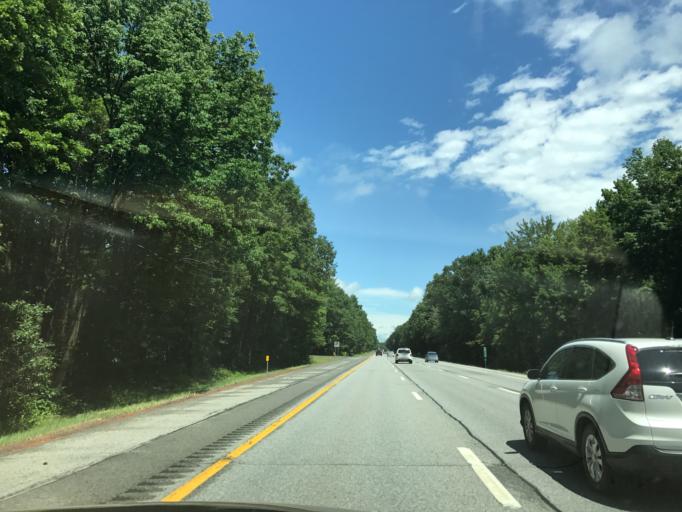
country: US
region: New York
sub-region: Saratoga County
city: Saratoga Springs
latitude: 43.1417
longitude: -73.7287
